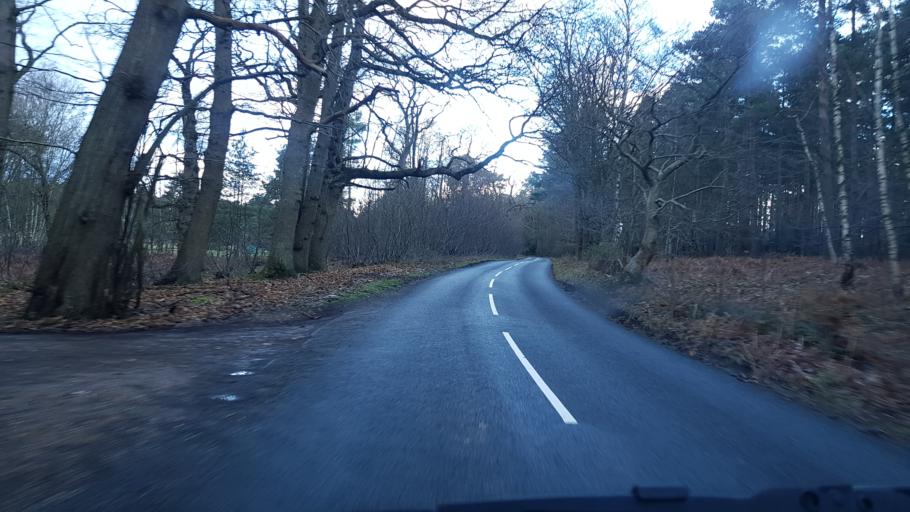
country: GB
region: England
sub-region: Surrey
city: Elstead
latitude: 51.1997
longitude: -0.7186
